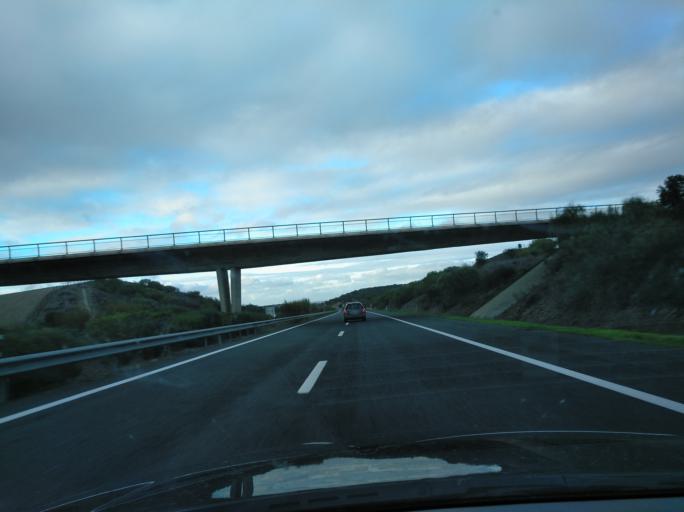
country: PT
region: Beja
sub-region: Aljustrel
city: Aljustrel
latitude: 37.8622
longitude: -8.2304
